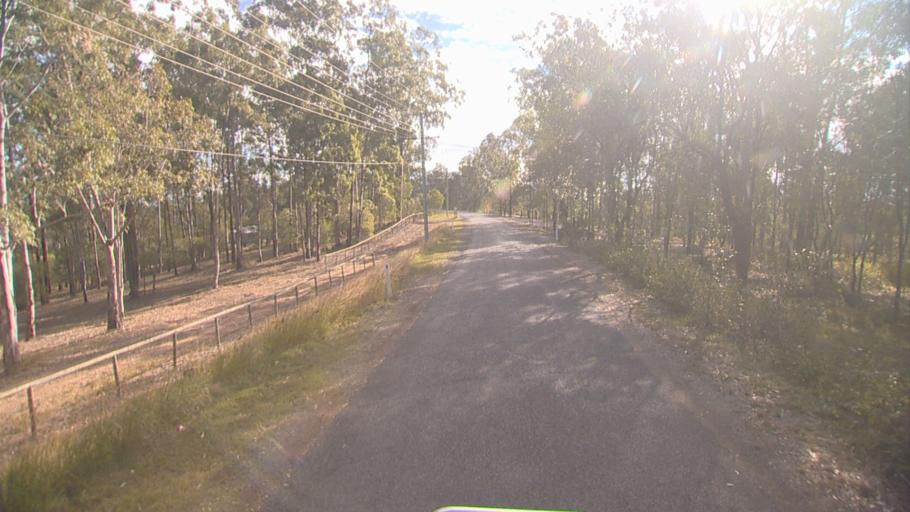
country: AU
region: Queensland
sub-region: Logan
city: Chambers Flat
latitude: -27.8249
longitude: 153.0754
